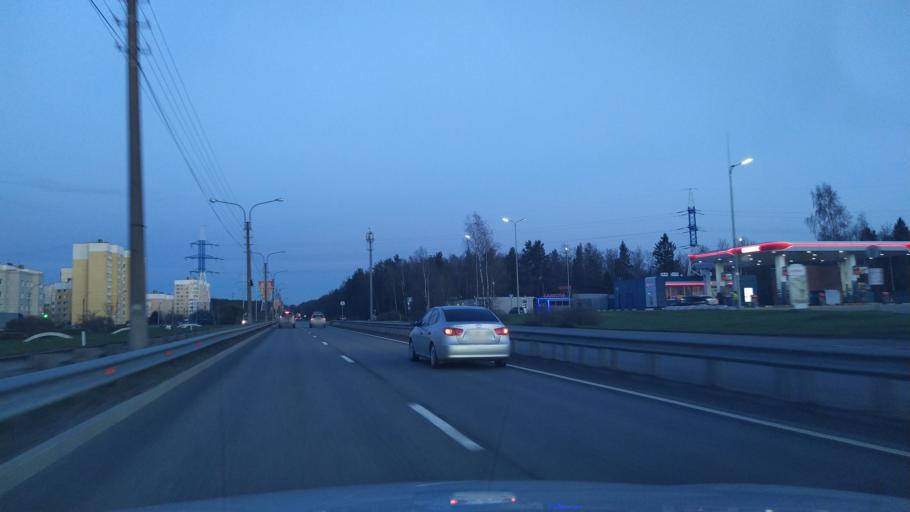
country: RU
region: St.-Petersburg
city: Razliv
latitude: 60.0813
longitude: 29.9594
